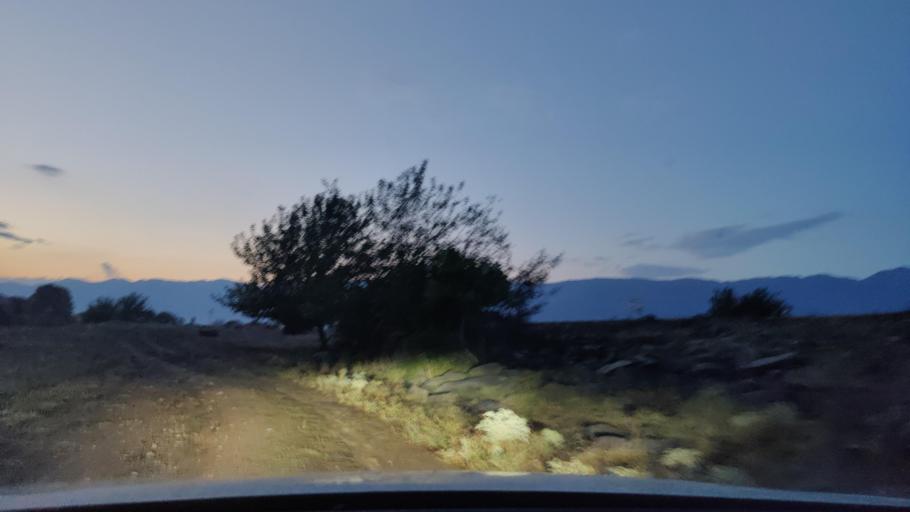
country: GR
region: Central Macedonia
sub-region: Nomos Serron
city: Chrysochorafa
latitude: 41.2041
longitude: 23.0783
